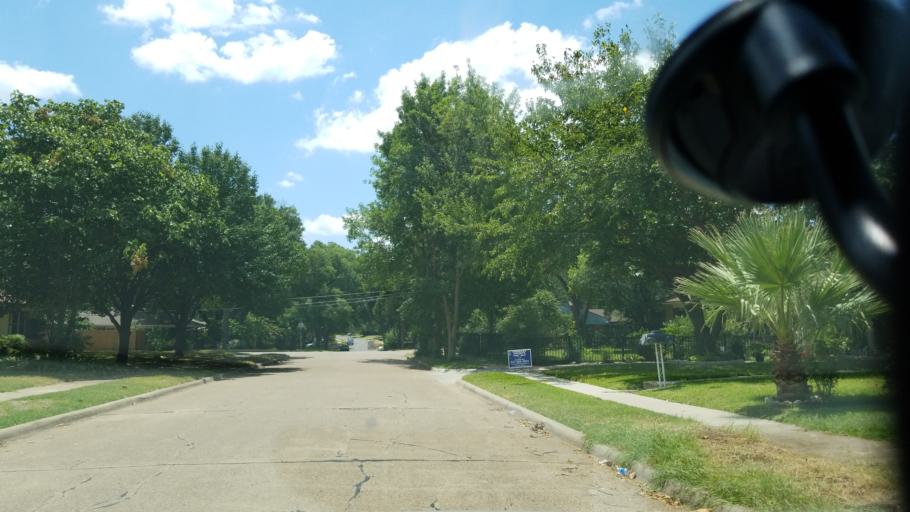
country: US
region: Texas
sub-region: Dallas County
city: Cockrell Hill
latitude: 32.7097
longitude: -96.8474
